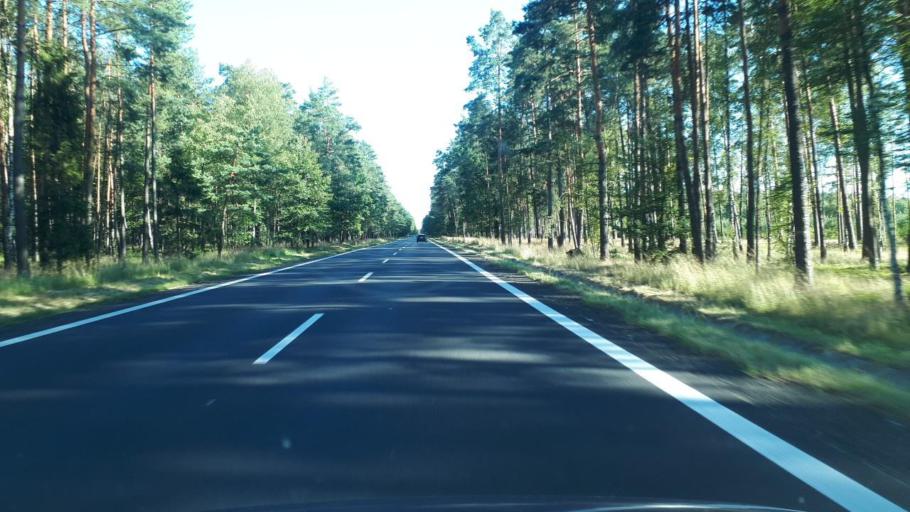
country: PL
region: Silesian Voivodeship
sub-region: Powiat tarnogorski
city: Tworog
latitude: 50.5665
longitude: 18.7120
